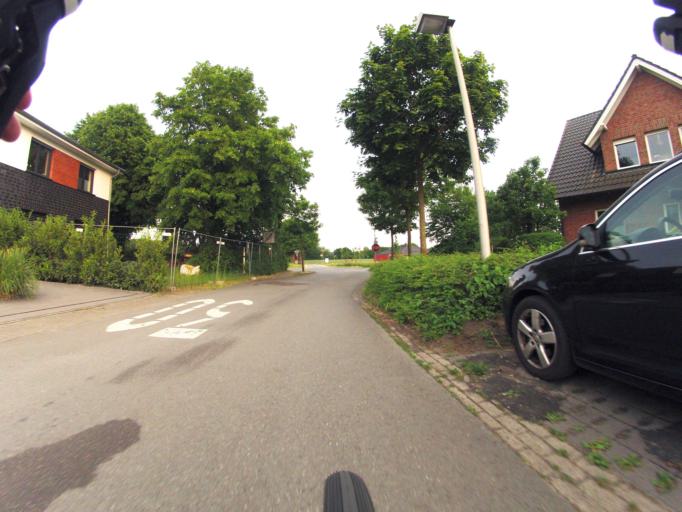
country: DE
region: North Rhine-Westphalia
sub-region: Regierungsbezirk Munster
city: Tecklenburg
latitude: 52.2670
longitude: 7.7958
